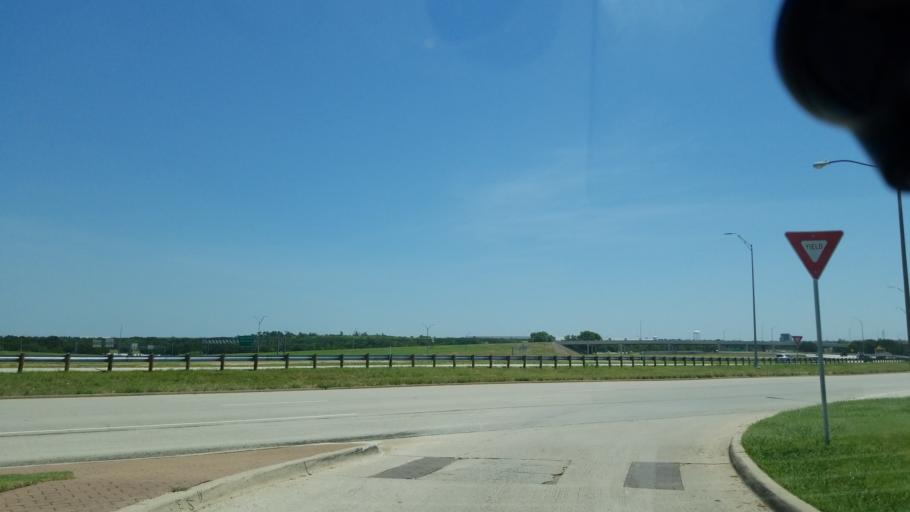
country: US
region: Texas
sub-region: Tarrant County
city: Euless
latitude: 32.8354
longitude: -97.0458
